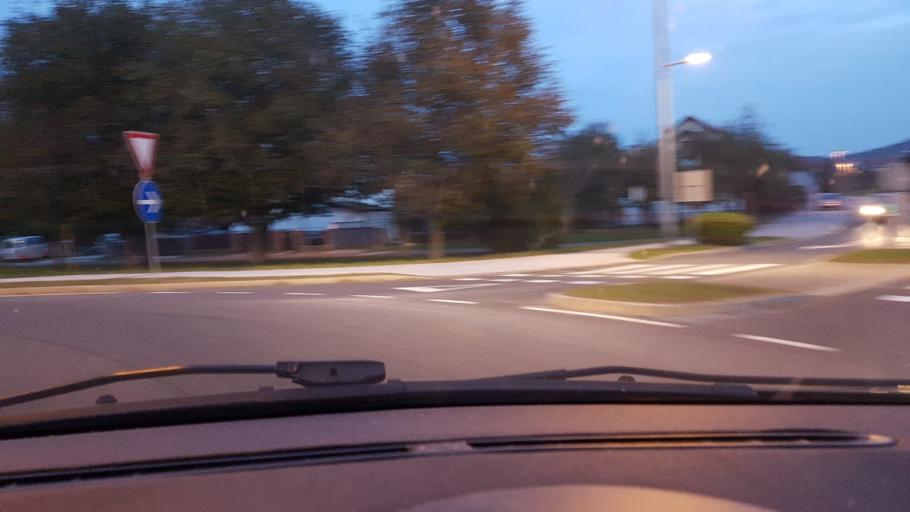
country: HR
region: Varazdinska
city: Ivanec
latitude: 46.2261
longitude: 16.1146
